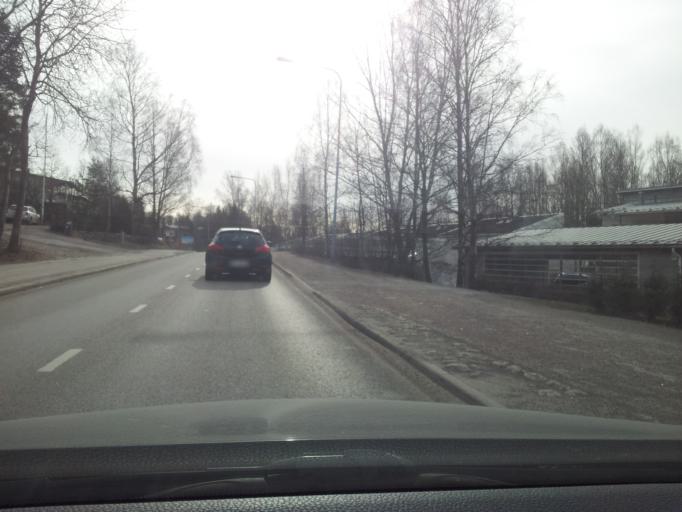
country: FI
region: Uusimaa
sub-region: Helsinki
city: Kilo
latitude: 60.1902
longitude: 24.7781
